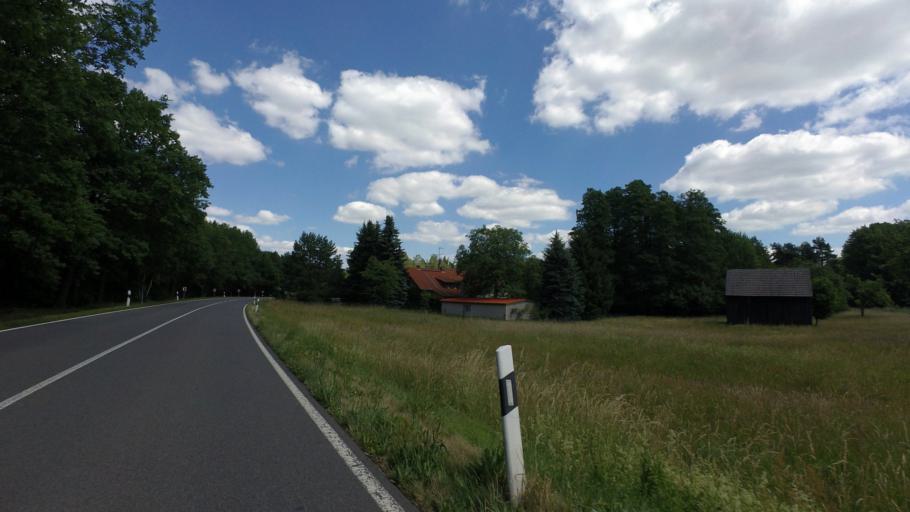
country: DE
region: Brandenburg
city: Sonnewalde
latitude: 51.7529
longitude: 13.6781
